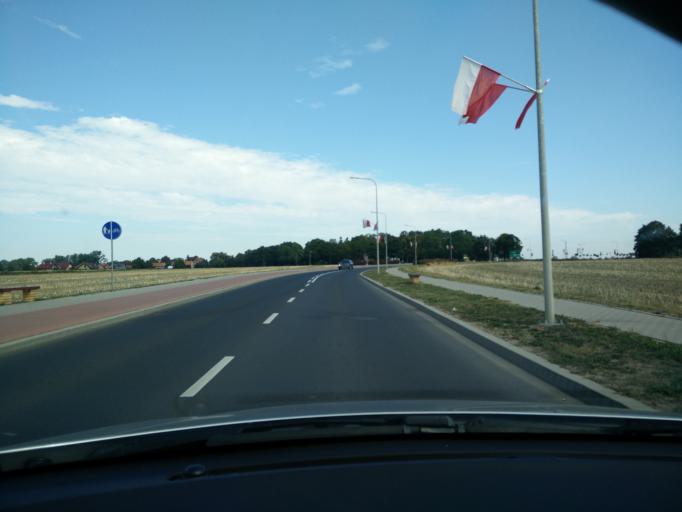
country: PL
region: Greater Poland Voivodeship
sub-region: Powiat sredzki
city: Sroda Wielkopolska
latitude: 52.2373
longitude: 17.2715
